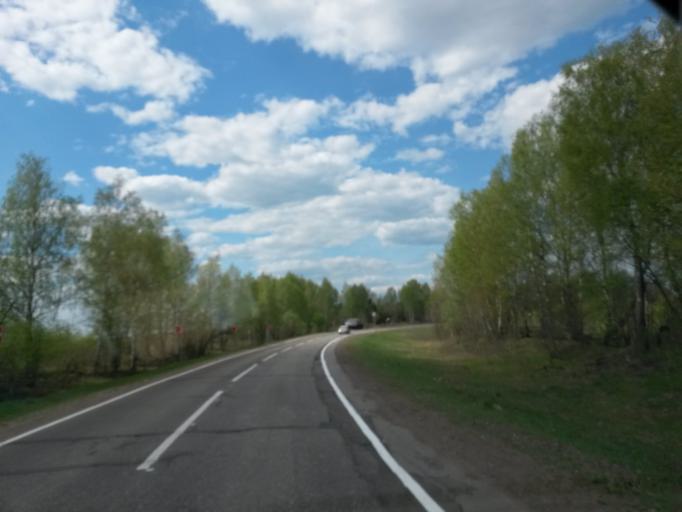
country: RU
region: Jaroslavl
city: Bol'shoye Selo
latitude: 57.6873
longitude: 39.2013
